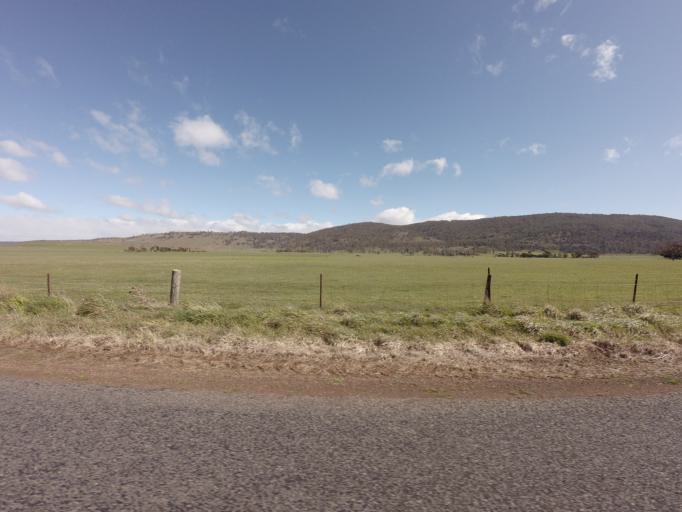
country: AU
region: Tasmania
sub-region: Northern Midlands
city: Evandale
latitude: -41.9864
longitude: 147.4510
